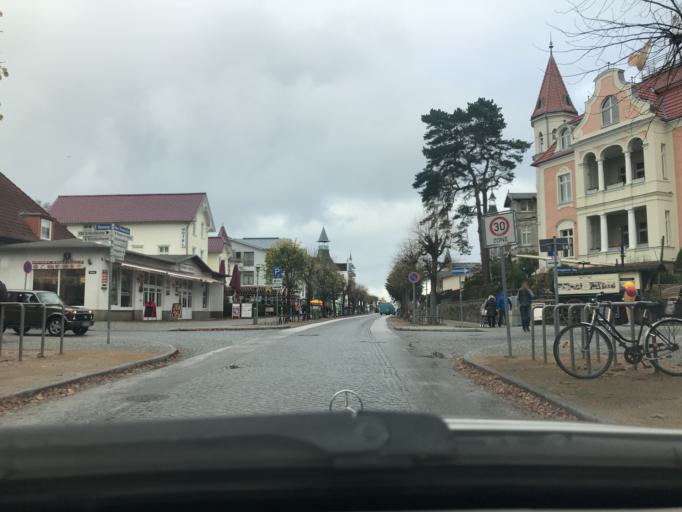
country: DE
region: Mecklenburg-Vorpommern
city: Ostseebad Zinnowitz
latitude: 54.0790
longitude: 13.9134
